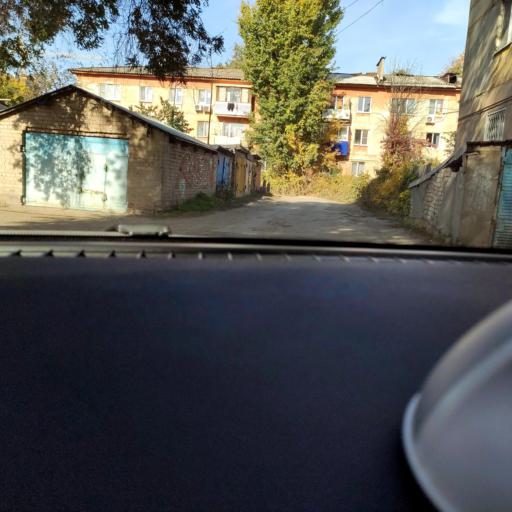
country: RU
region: Samara
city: Smyshlyayevka
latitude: 53.2009
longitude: 50.2886
